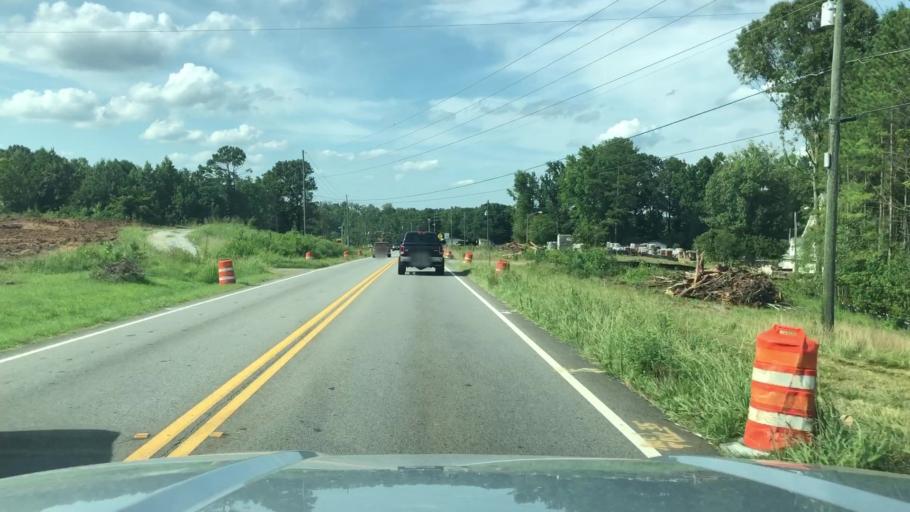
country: US
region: Georgia
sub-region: Paulding County
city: Hiram
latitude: 33.8483
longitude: -84.7568
